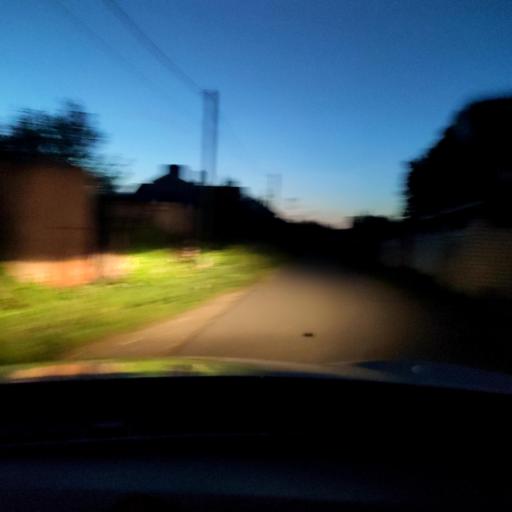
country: RU
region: Tatarstan
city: Osinovo
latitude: 55.8506
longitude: 48.9104
